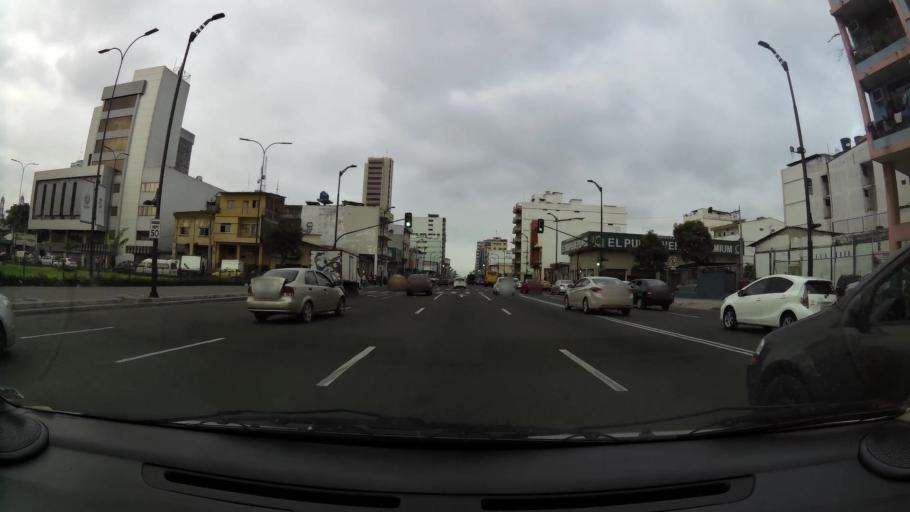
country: EC
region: Guayas
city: Guayaquil
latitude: -2.1861
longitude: -79.8890
